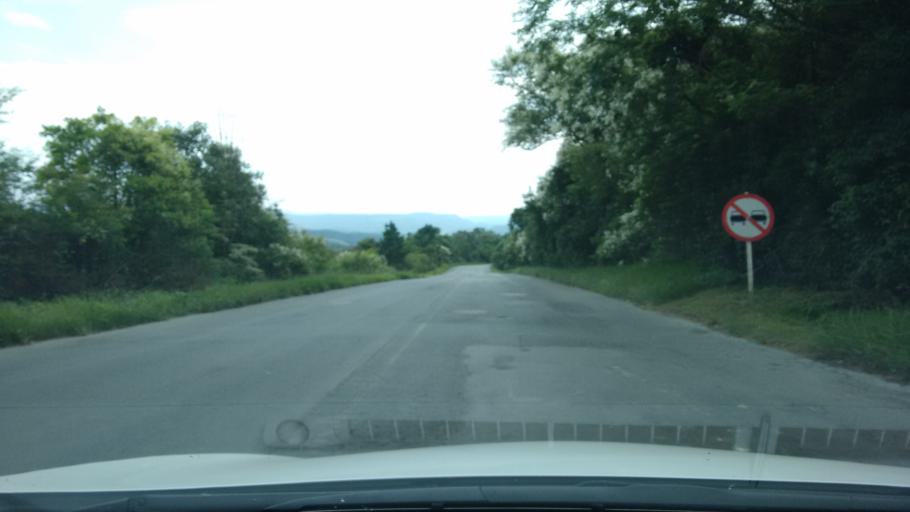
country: BR
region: Santa Catarina
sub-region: Otacilio Costa
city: Otacilio Costa
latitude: -27.2718
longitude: -50.0624
